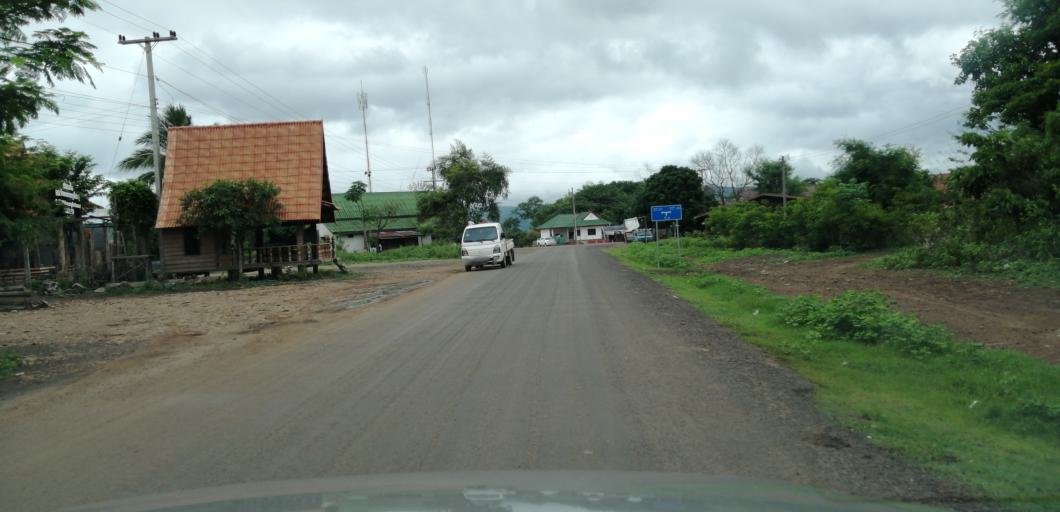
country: LA
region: Xekong
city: Lamam
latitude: 15.1666
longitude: 106.7647
